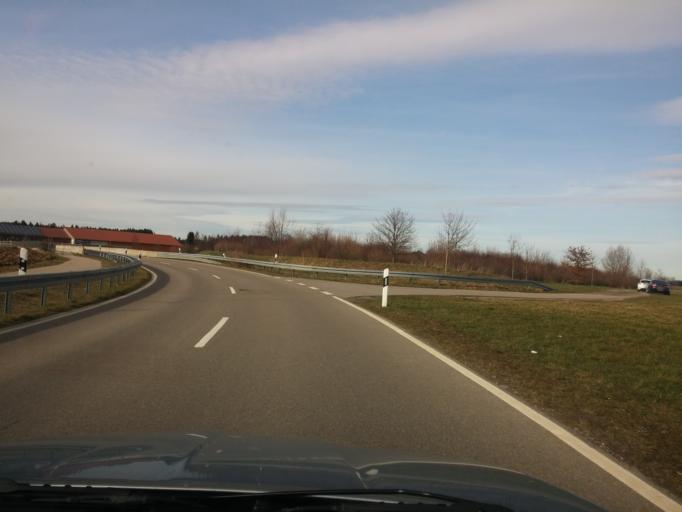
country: DE
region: Bavaria
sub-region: Swabia
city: Trunkelsberg
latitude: 47.9980
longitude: 10.2223
